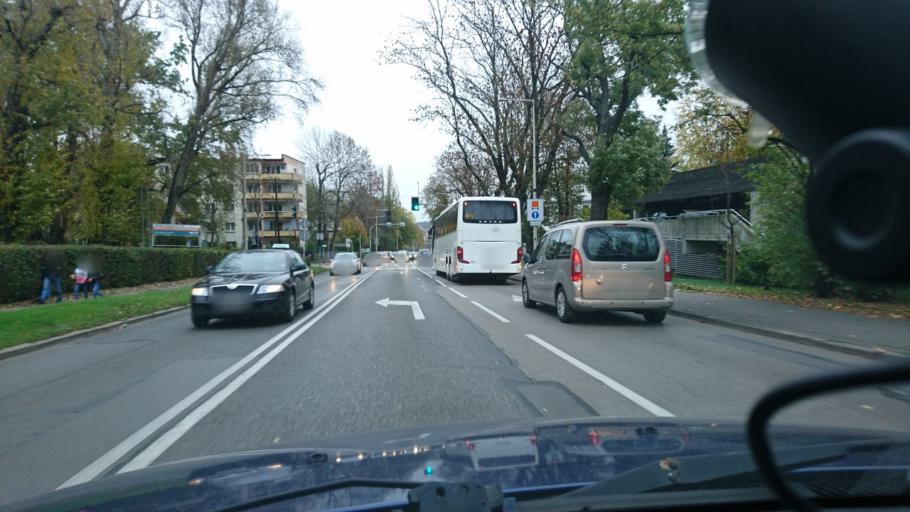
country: PL
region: Silesian Voivodeship
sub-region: Bielsko-Biala
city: Bielsko-Biala
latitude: 49.8276
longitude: 19.0378
